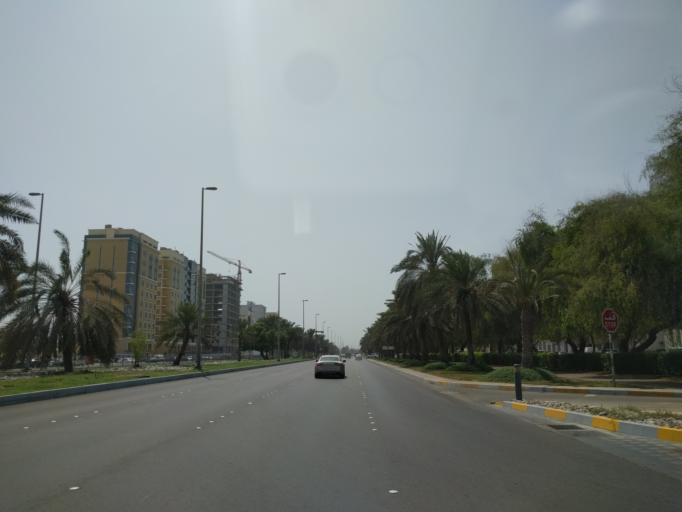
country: AE
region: Abu Dhabi
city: Abu Dhabi
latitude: 24.4391
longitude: 54.4133
